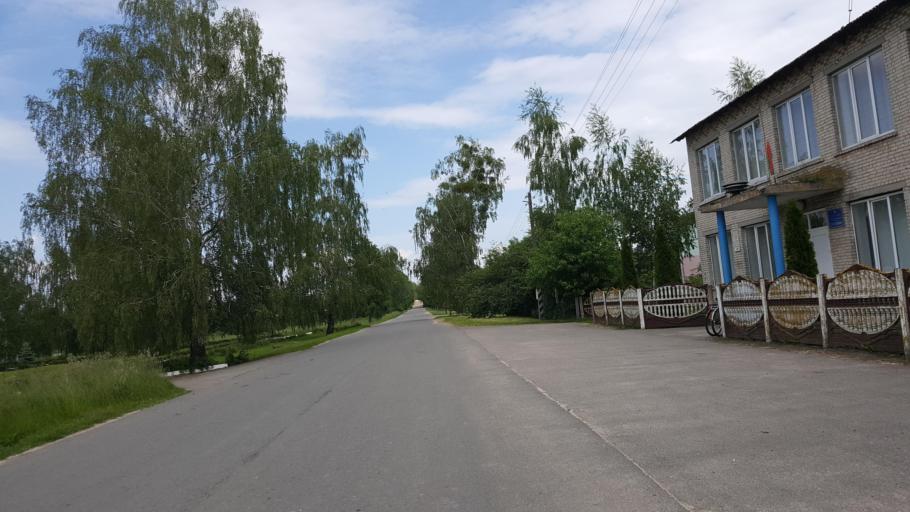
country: PL
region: Podlasie
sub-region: Powiat hajnowski
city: Bialowieza
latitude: 52.6715
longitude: 24.0857
